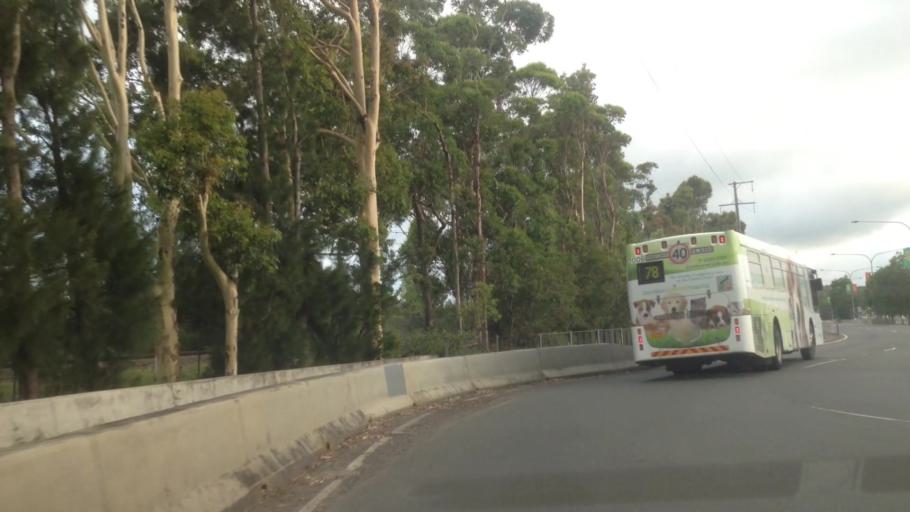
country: AU
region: New South Wales
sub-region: Wyong Shire
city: Chittaway Bay
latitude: -33.3033
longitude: 151.4209
